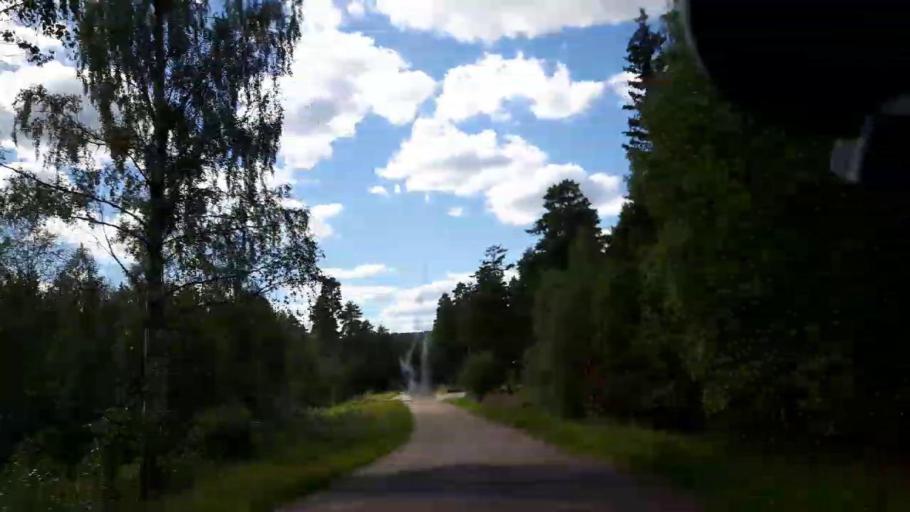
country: SE
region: Jaemtland
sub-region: Ragunda Kommun
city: Hammarstrand
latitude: 63.0117
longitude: 16.6466
